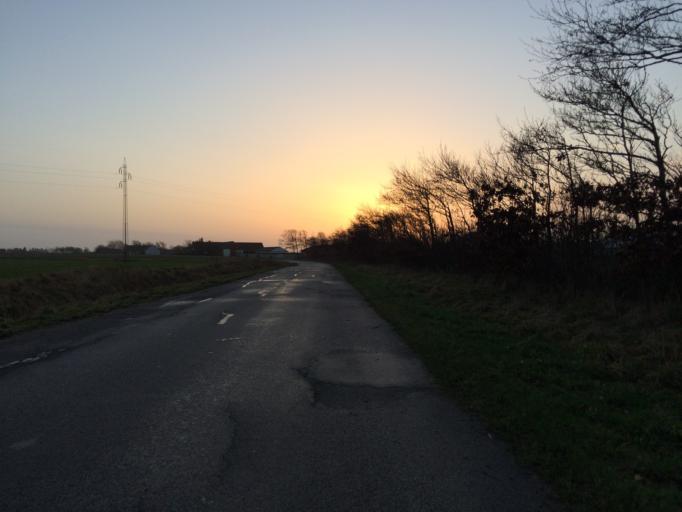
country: DK
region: Central Jutland
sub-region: Holstebro Kommune
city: Ulfborg
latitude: 56.2835
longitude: 8.2880
